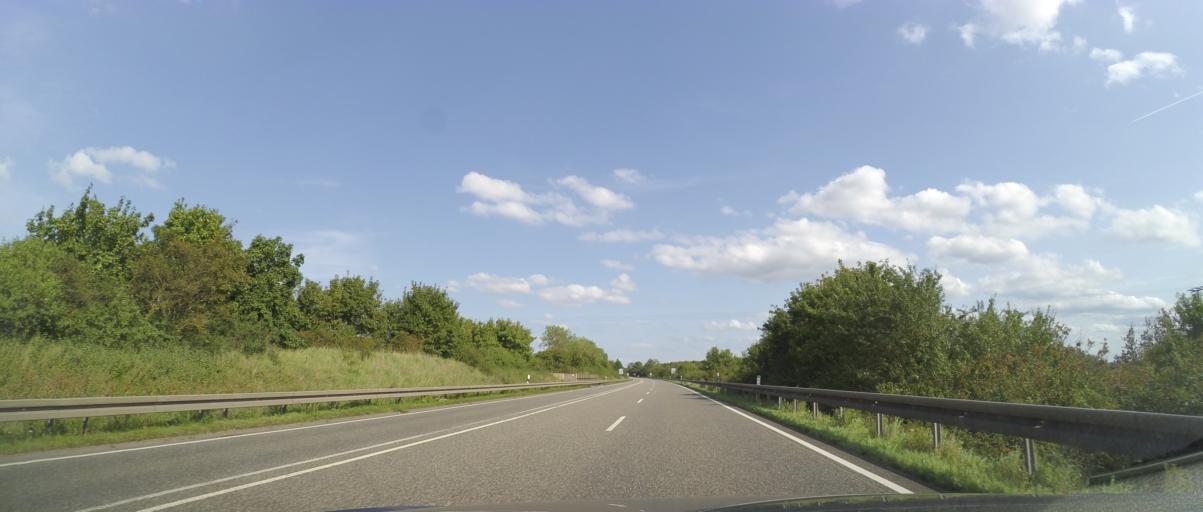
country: DE
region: North Rhine-Westphalia
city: Zulpich
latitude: 50.6803
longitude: 6.7209
